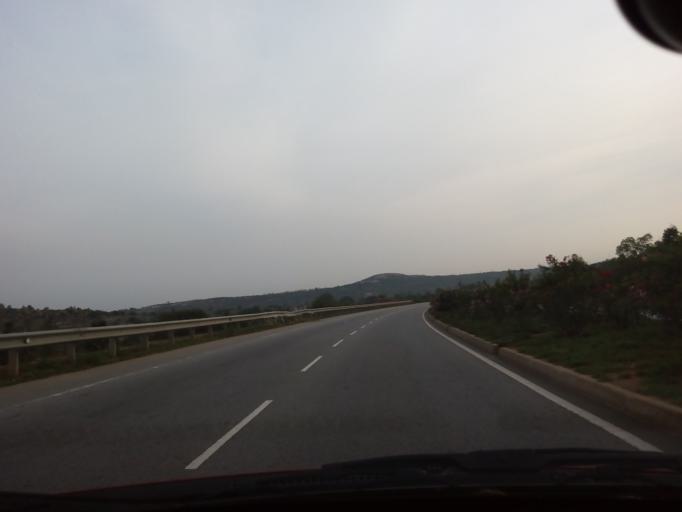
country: IN
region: Karnataka
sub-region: Chikkaballapur
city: Chik Ballapur
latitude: 13.5314
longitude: 77.7655
